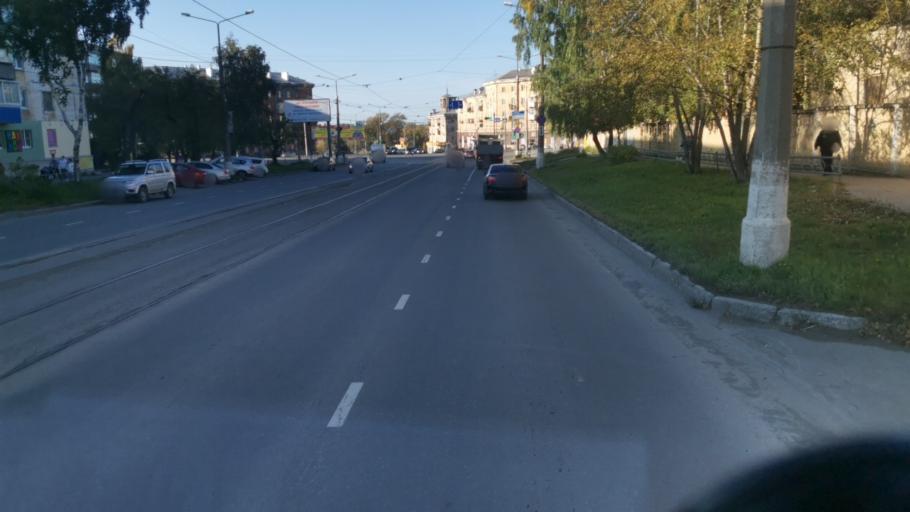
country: RU
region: Sverdlovsk
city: Nizhniy Tagil
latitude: 57.9237
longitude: 59.9408
